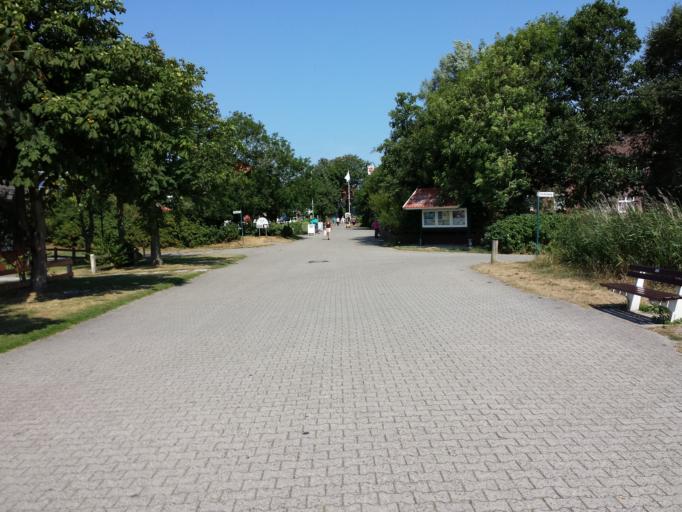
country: DE
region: Lower Saxony
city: Spiekeroog
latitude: 53.7688
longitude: 7.6940
